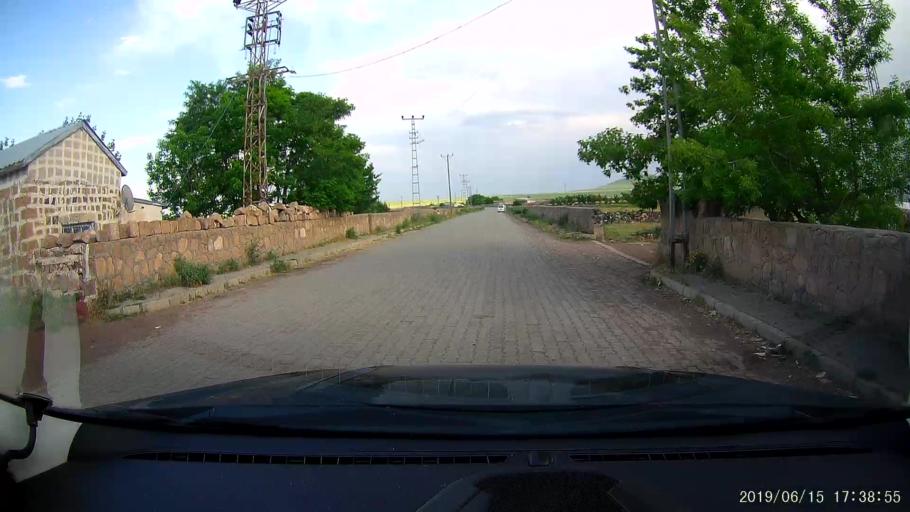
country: TR
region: Kars
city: Basgedikler
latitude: 40.5186
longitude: 43.5686
